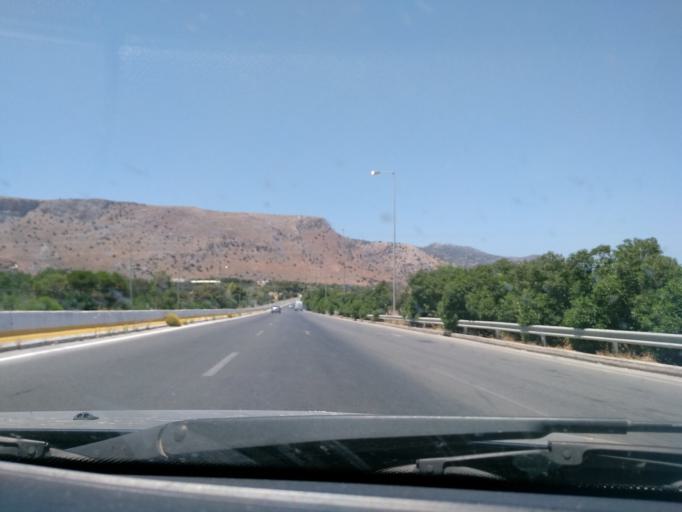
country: GR
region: Crete
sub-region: Nomos Irakleiou
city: Gazi
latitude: 35.3215
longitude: 25.0636
